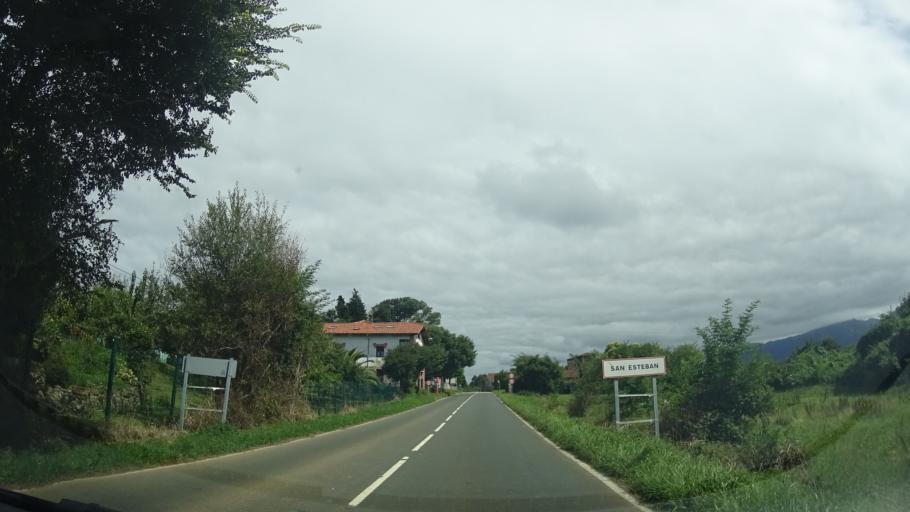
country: ES
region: Asturias
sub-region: Province of Asturias
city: Ribadesella
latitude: 43.4644
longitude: -5.1119
